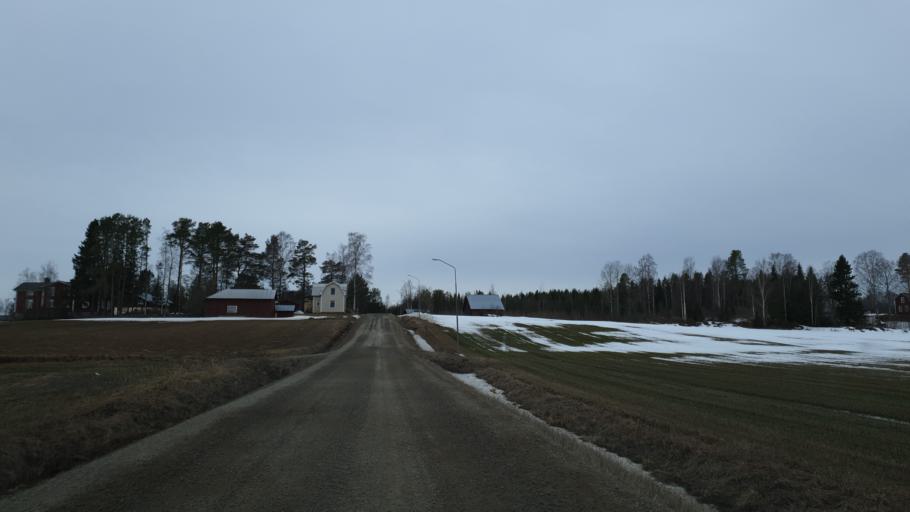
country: SE
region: Vaesterbotten
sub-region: Robertsfors Kommun
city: Robertsfors
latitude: 64.3782
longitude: 20.9078
